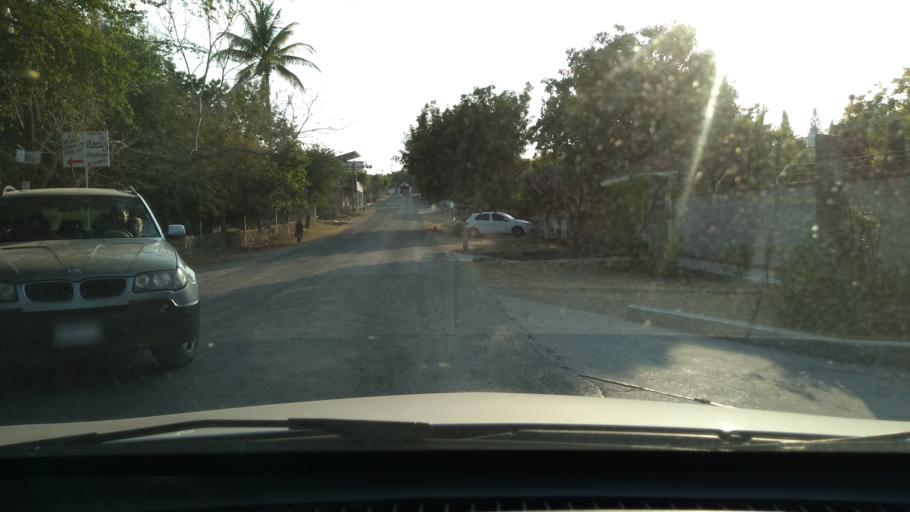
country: MX
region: Morelos
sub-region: Jojutla
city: Tehuixtla
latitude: 18.5634
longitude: -99.2721
